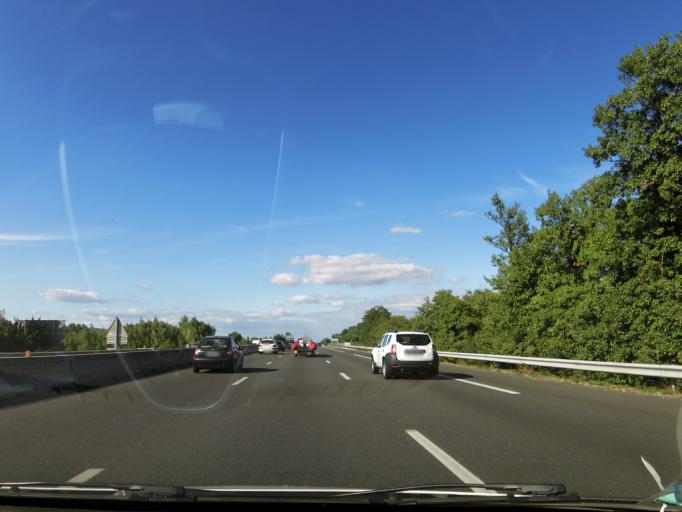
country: FR
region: Rhone-Alpes
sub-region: Departement de la Drome
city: Loriol-sur-Drome
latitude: 44.7652
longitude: 4.7983
